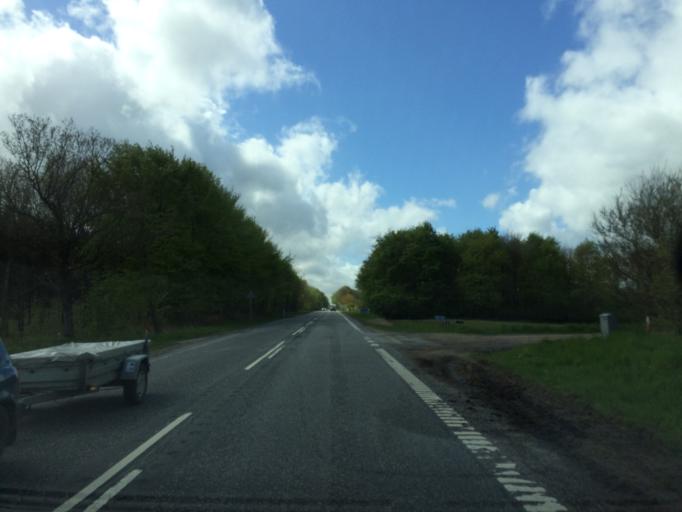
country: DK
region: Central Jutland
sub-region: Viborg Kommune
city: Stoholm
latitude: 56.4270
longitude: 9.0924
